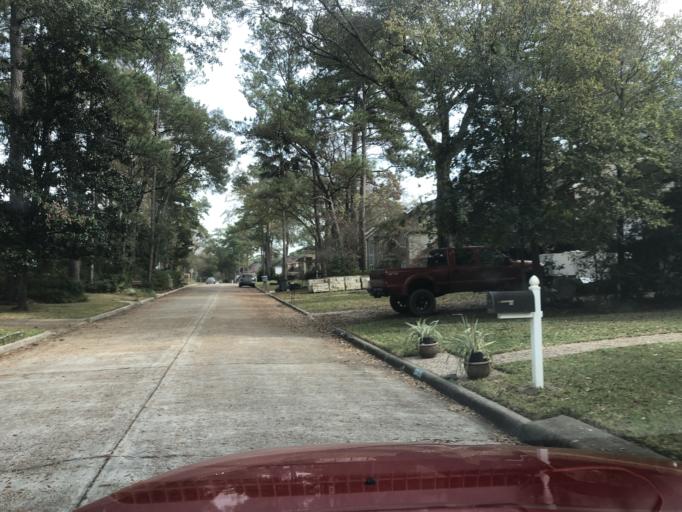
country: US
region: Texas
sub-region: Harris County
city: Spring
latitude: 30.0178
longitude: -95.4674
